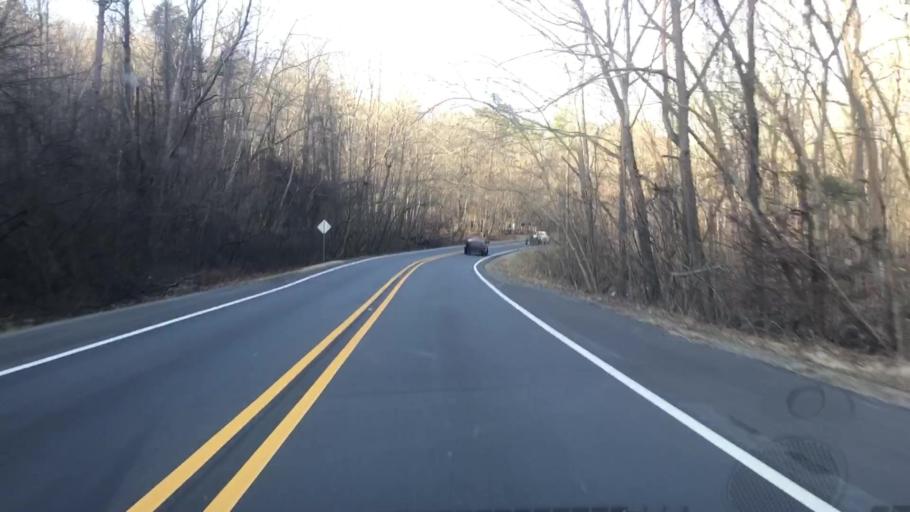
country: US
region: Arkansas
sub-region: Montgomery County
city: Mount Ida
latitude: 34.5229
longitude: -93.3970
